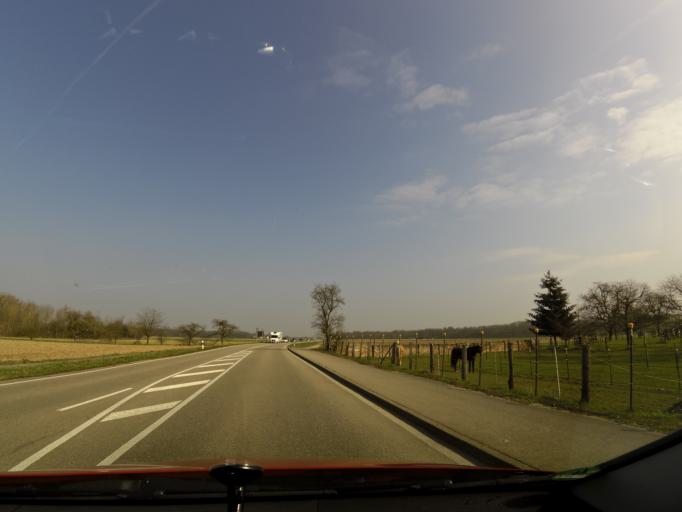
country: DE
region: Baden-Wuerttemberg
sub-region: Freiburg Region
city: Willstatt
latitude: 48.6045
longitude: 7.8818
